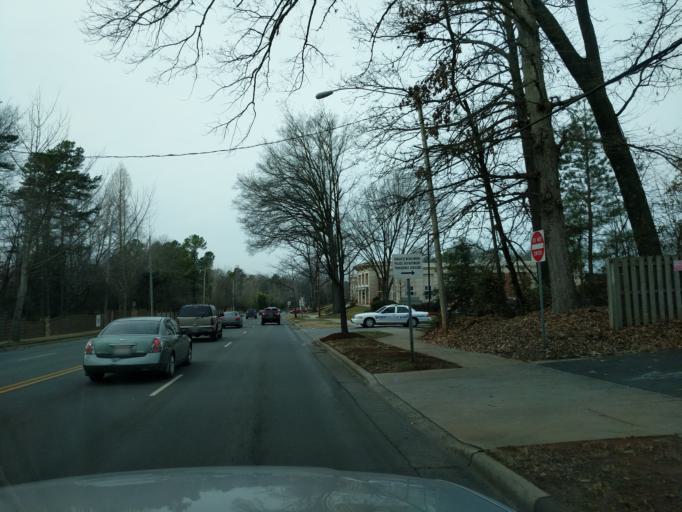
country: US
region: North Carolina
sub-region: Mecklenburg County
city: Charlotte
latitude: 35.1897
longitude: -80.7995
